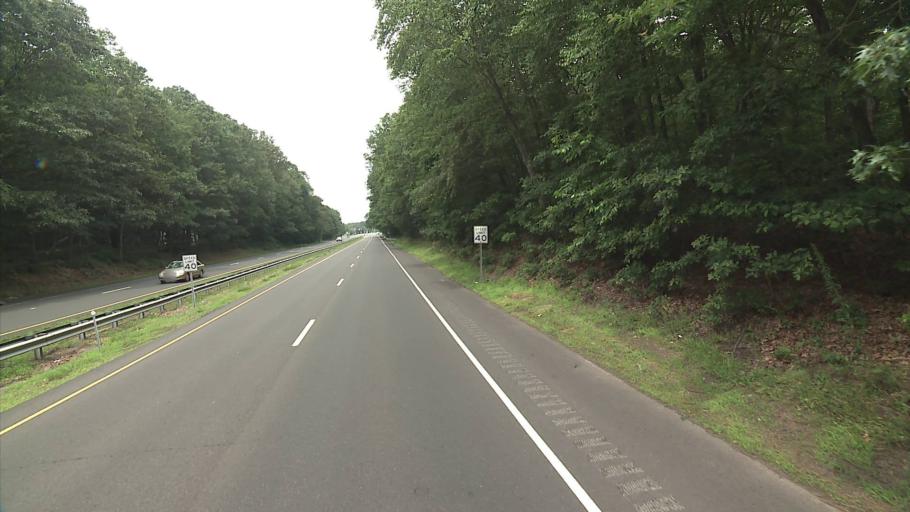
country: US
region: Connecticut
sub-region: New Haven County
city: Madison
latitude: 41.2866
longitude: -72.5679
